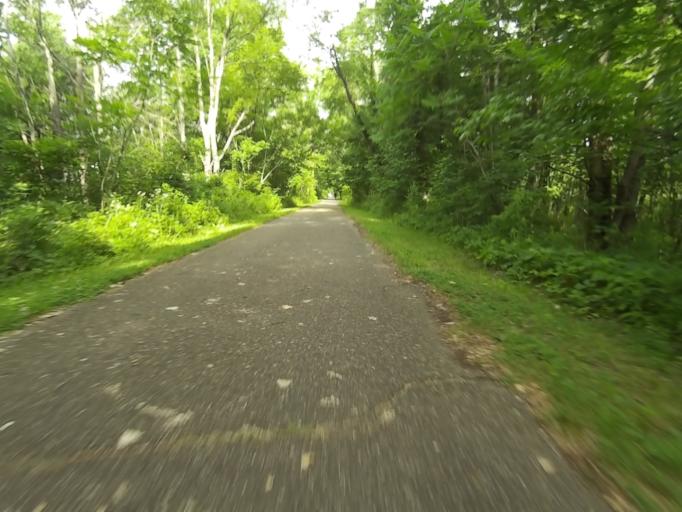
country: US
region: Ohio
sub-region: Portage County
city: Kent
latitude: 41.1857
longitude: -81.3719
